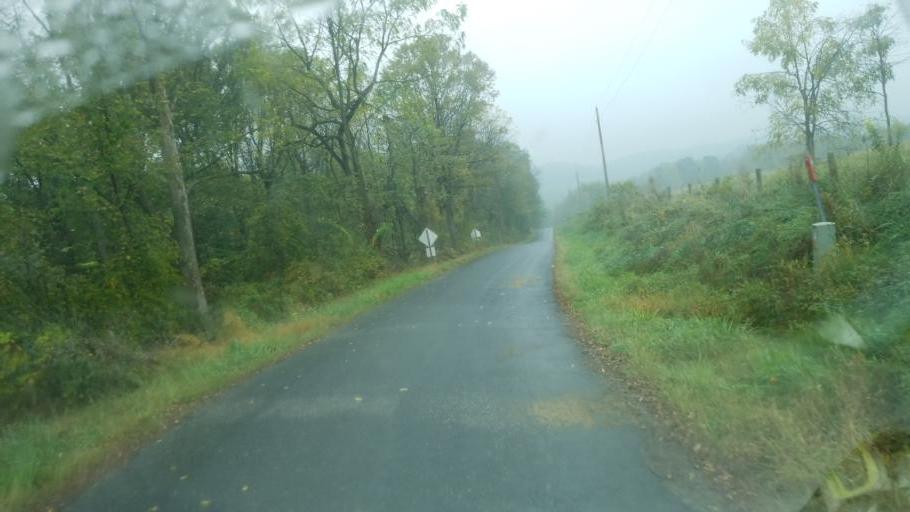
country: US
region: Ohio
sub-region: Tuscarawas County
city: Sugarcreek
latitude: 40.5784
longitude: -81.7409
